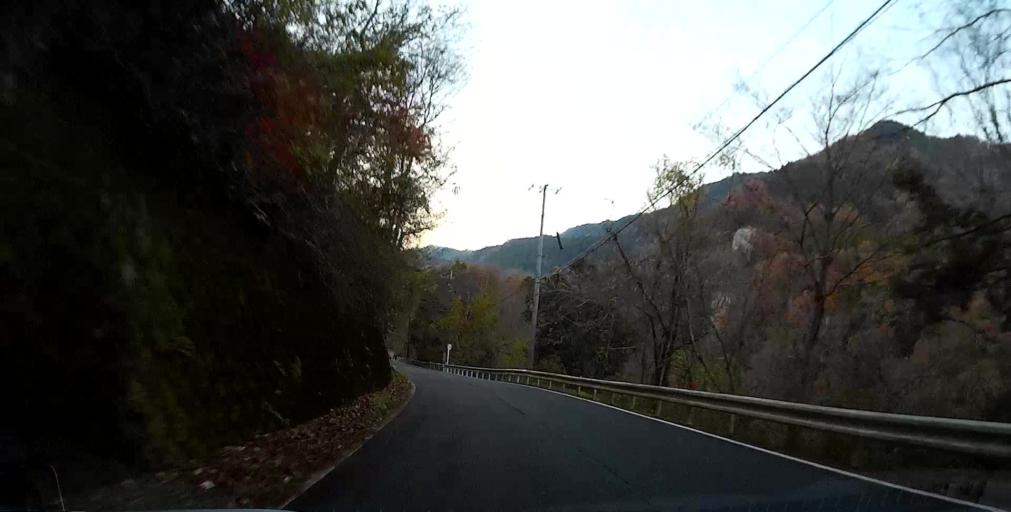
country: JP
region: Yamanashi
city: Uenohara
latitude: 35.5664
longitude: 139.2081
